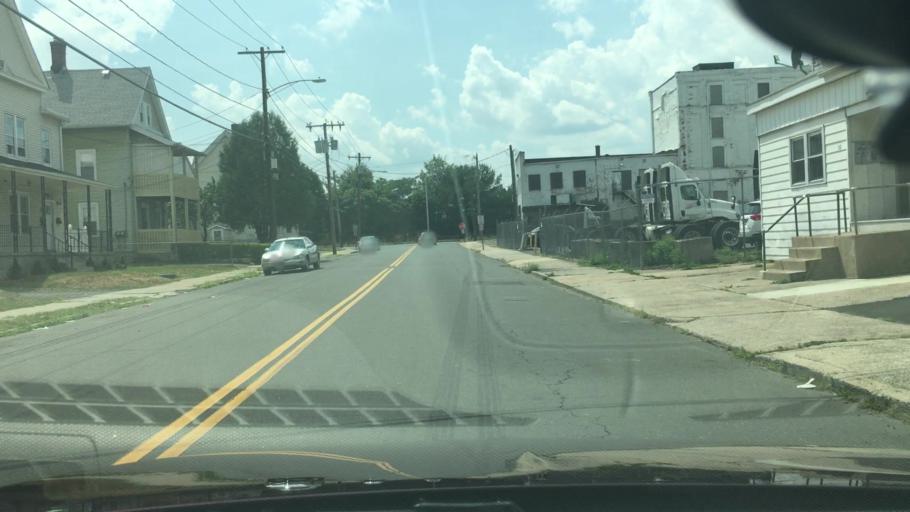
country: US
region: Connecticut
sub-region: Hartford County
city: New Britain
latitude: 41.6685
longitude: -72.7709
